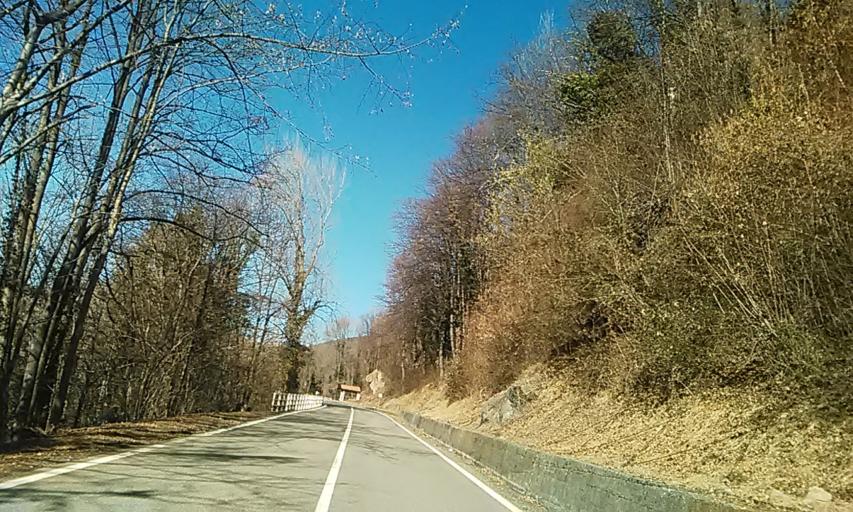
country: IT
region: Piedmont
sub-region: Provincia di Vercelli
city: Varallo
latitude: 45.8052
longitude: 8.2745
